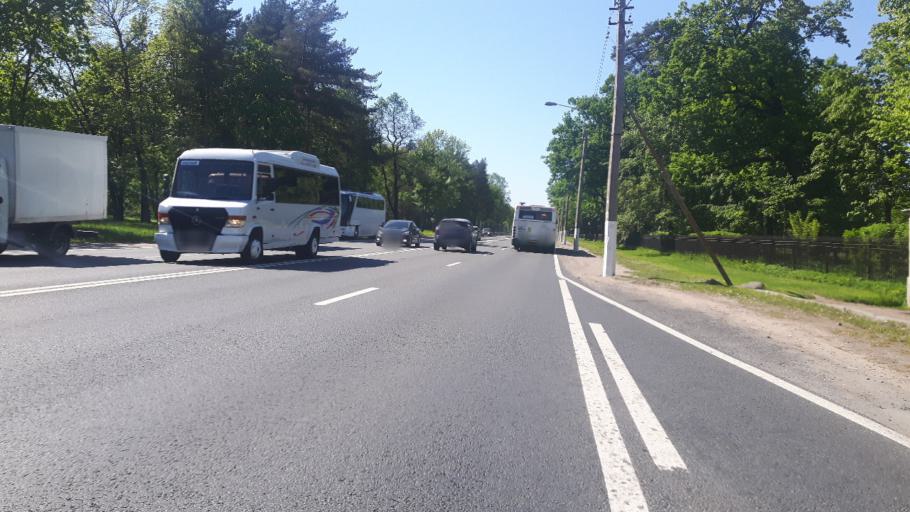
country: RU
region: Leningrad
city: Ol'gino
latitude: 59.8751
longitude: 29.9441
